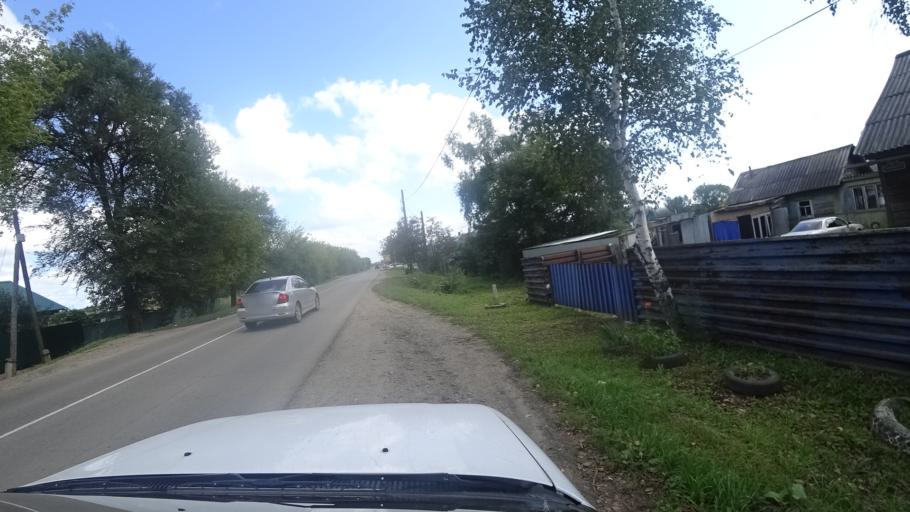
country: RU
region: Primorskiy
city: Dal'nerechensk
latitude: 45.9261
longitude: 133.7692
